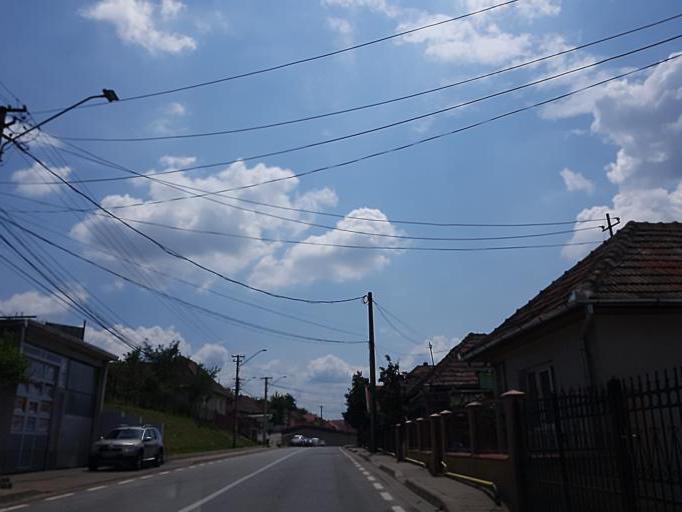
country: RO
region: Alba
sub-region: Municipiul Blaj
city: Veza
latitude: 46.1737
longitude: 23.9395
